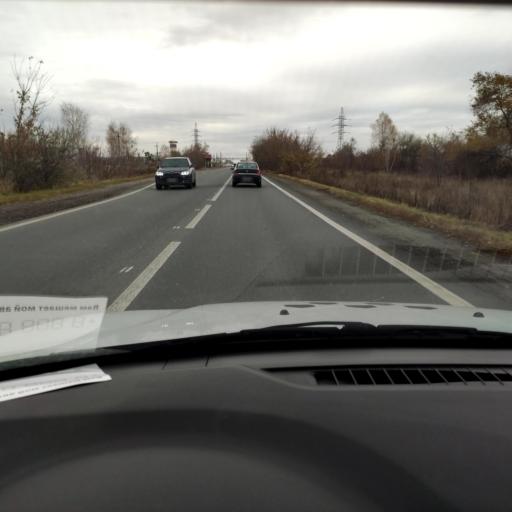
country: RU
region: Samara
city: Tol'yatti
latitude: 53.5476
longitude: 49.3768
